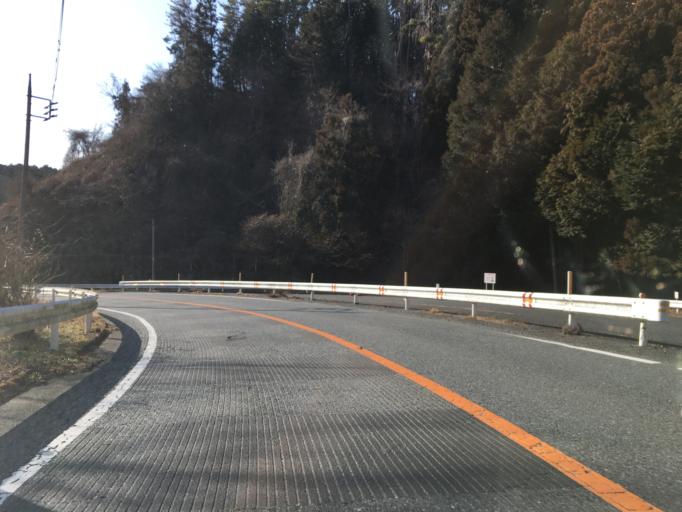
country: JP
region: Ibaraki
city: Hitachi
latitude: 36.7366
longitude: 140.5428
